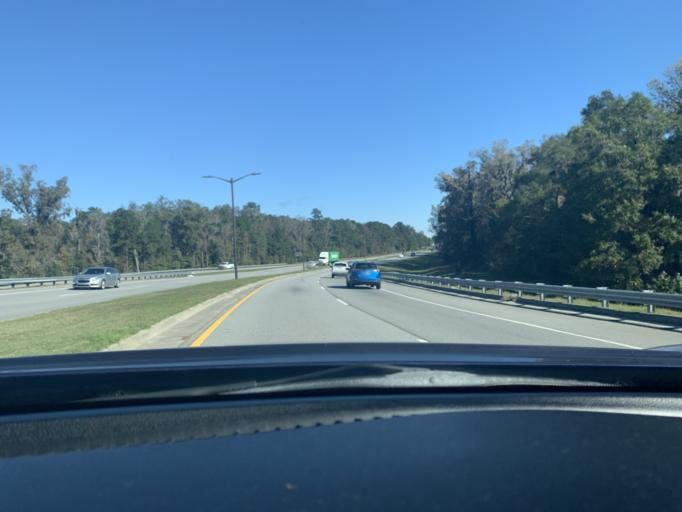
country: US
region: Georgia
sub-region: Chatham County
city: Pooler
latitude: 32.1245
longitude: -81.2665
